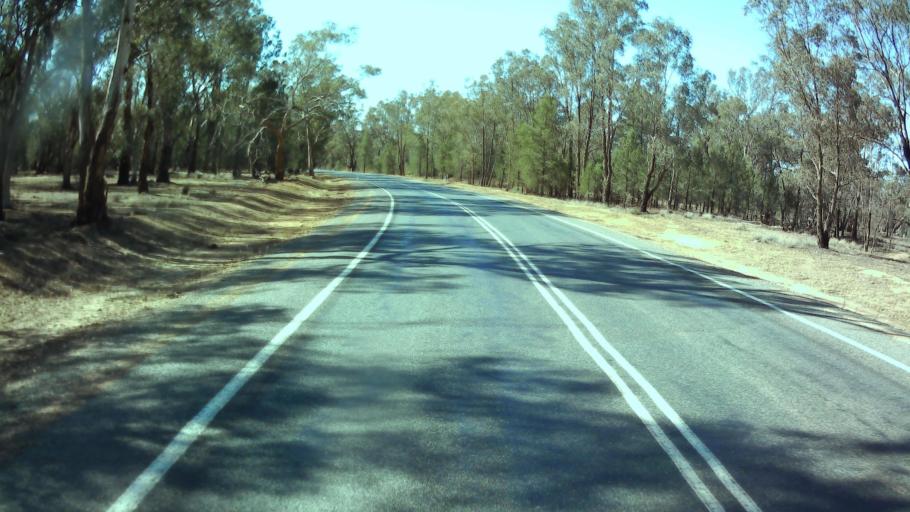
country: AU
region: New South Wales
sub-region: Weddin
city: Grenfell
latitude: -33.7293
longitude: 148.0887
